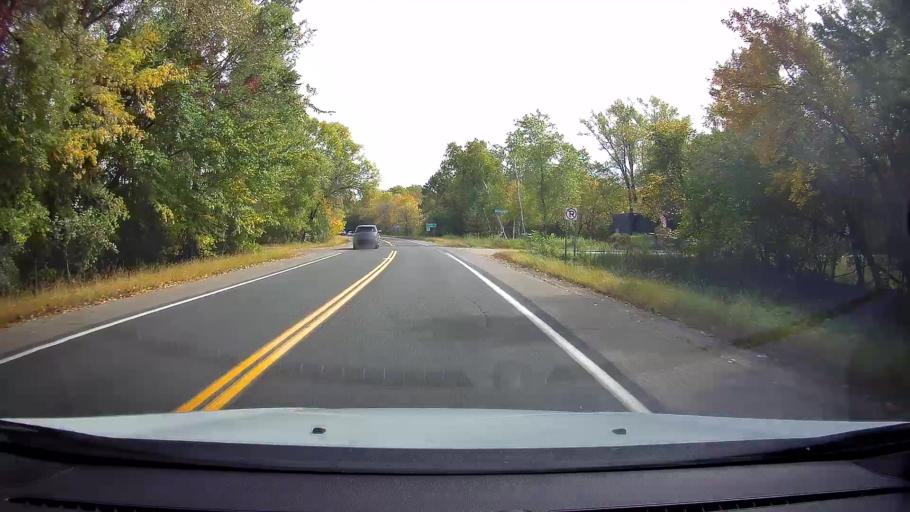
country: US
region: Minnesota
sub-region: Ramsey County
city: White Bear Lake
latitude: 45.0937
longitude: -93.0047
